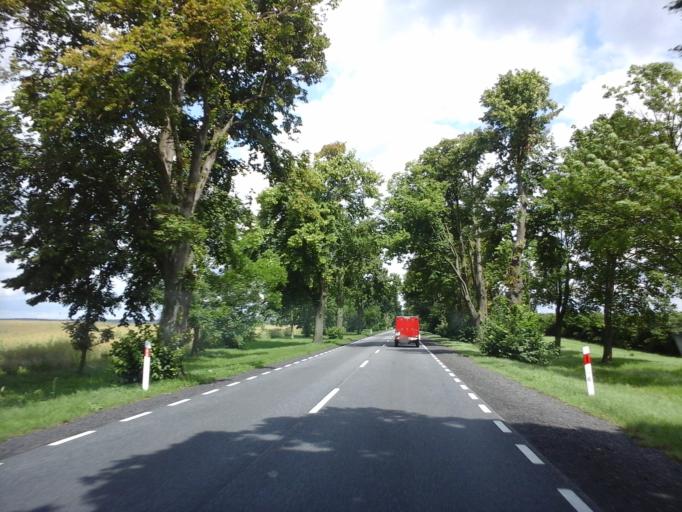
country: PL
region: Lubusz
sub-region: Powiat strzelecko-drezdenecki
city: Strzelce Krajenskie
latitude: 52.8941
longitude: 15.5750
